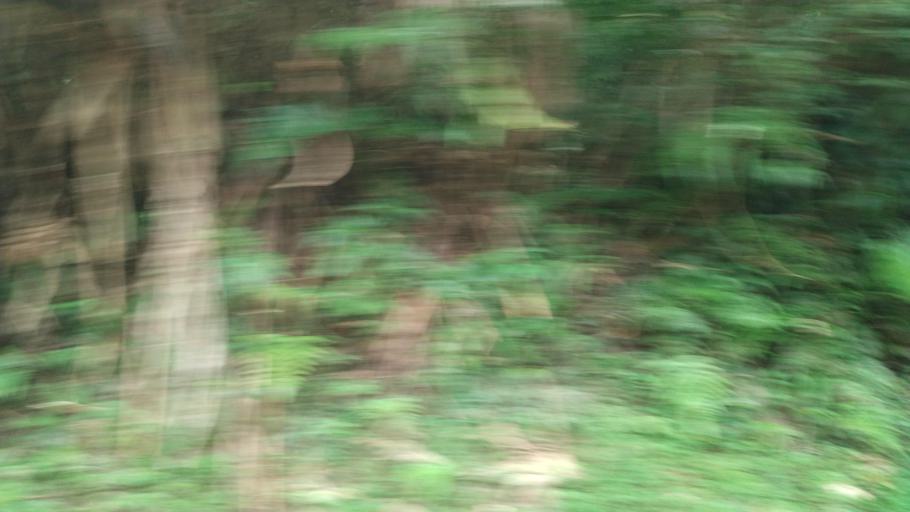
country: TW
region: Taiwan
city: Daxi
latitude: 24.9115
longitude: 121.3987
